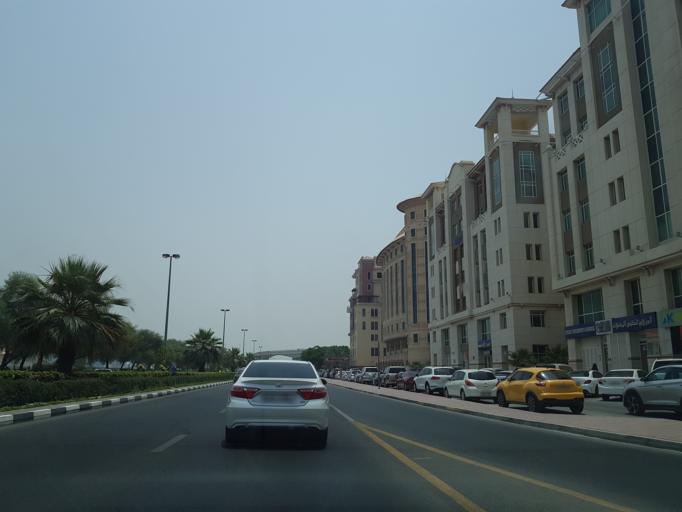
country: AE
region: Ash Shariqah
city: Sharjah
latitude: 25.2334
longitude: 55.3262
